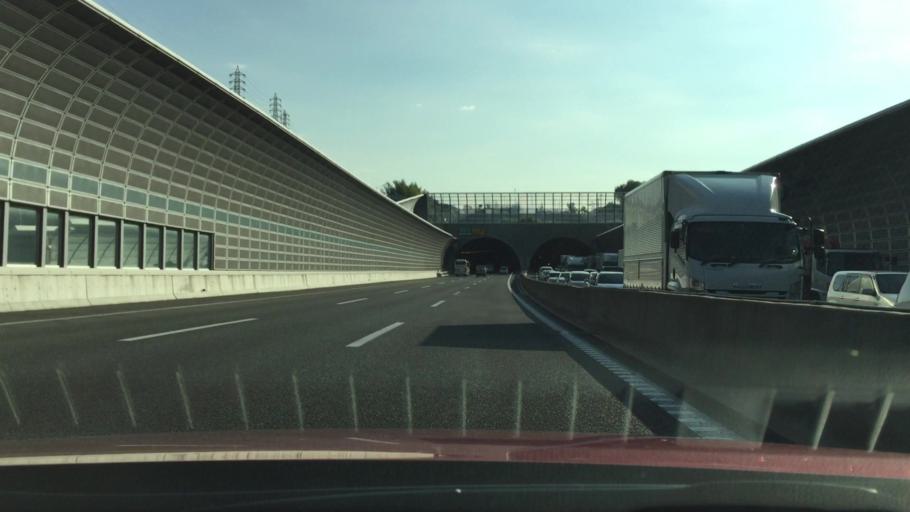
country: JP
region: Osaka
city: Neyagawa
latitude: 34.7535
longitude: 135.6374
